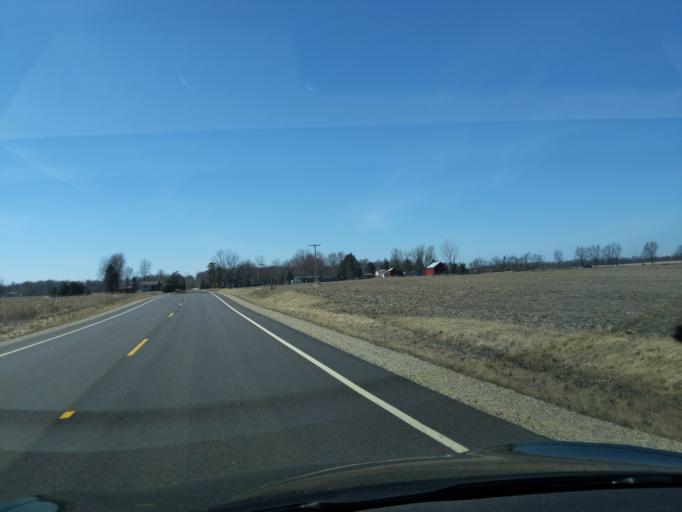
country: US
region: Michigan
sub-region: Ionia County
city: Lake Odessa
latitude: 42.7270
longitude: -85.0297
